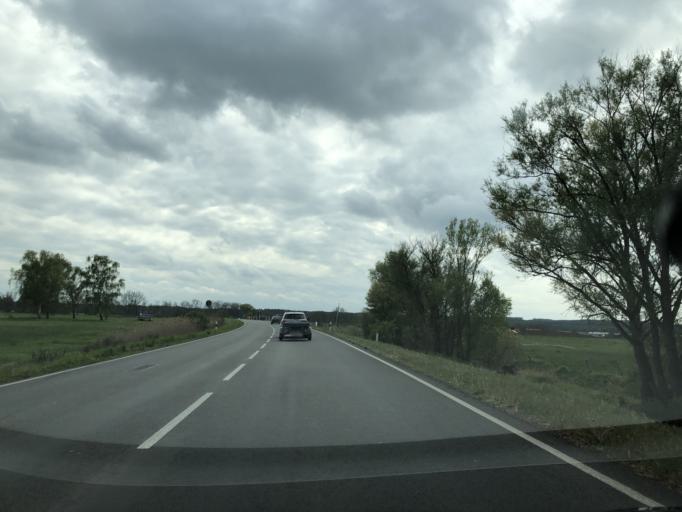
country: DE
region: Saxony-Anhalt
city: Luderitz
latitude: 52.5078
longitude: 11.7334
